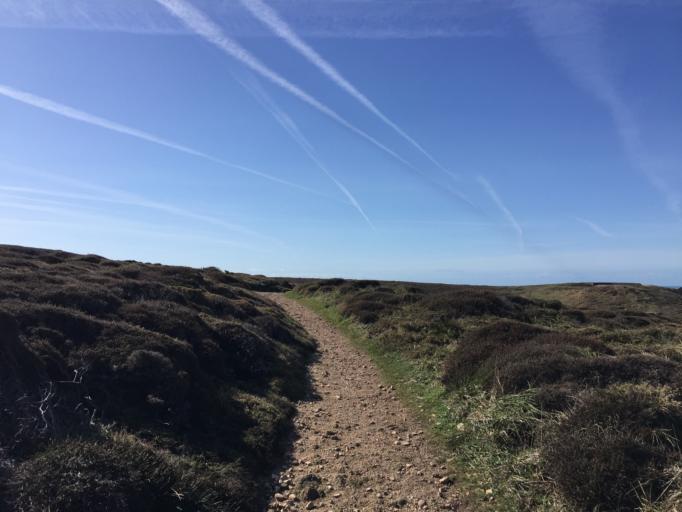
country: JE
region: St Helier
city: Saint Helier
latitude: 49.2538
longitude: -2.2502
